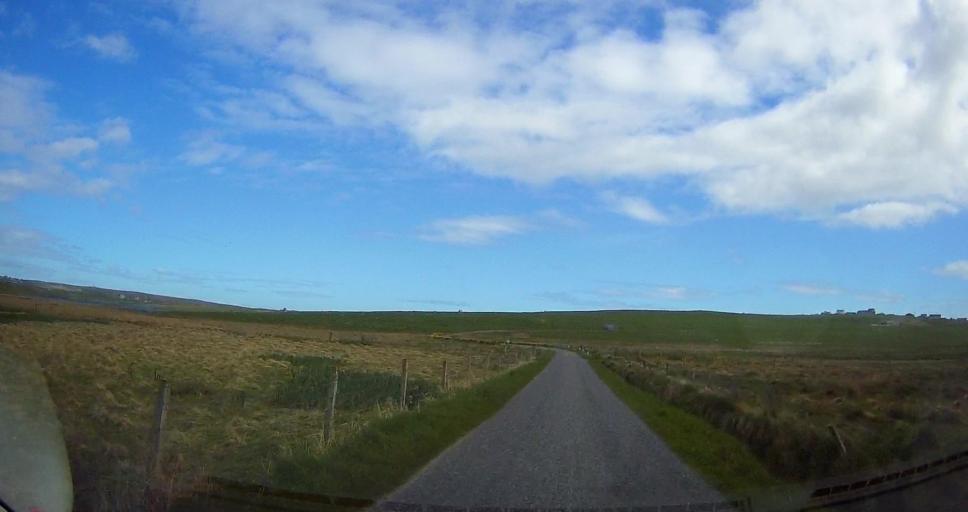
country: GB
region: Scotland
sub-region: Shetland Islands
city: Sandwick
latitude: 59.9226
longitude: -1.3282
